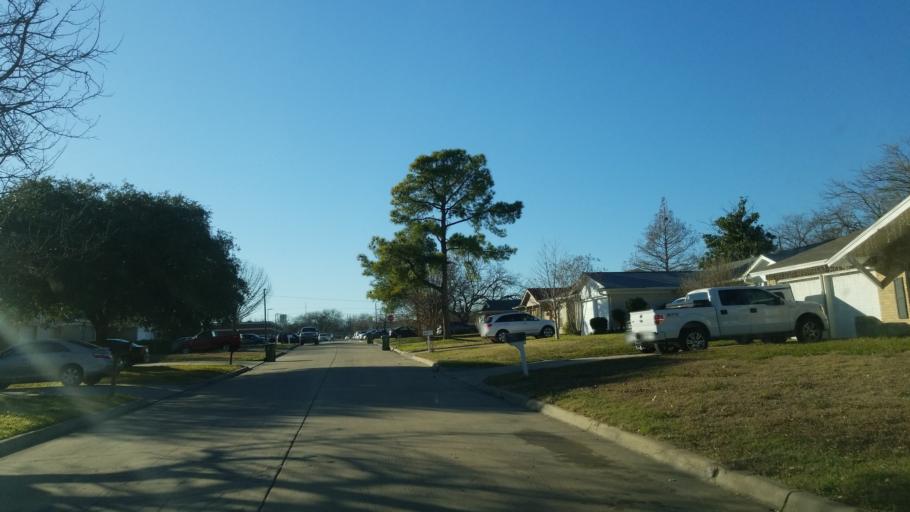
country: US
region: Texas
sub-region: Tarrant County
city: Arlington
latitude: 32.7224
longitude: -97.0654
